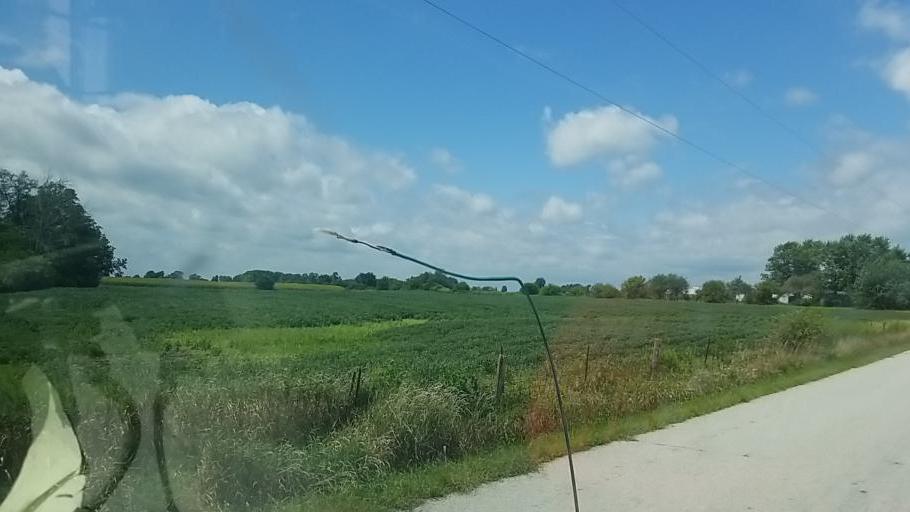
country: US
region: Ohio
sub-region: Clark County
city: South Charleston
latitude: 39.7475
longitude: -83.6728
